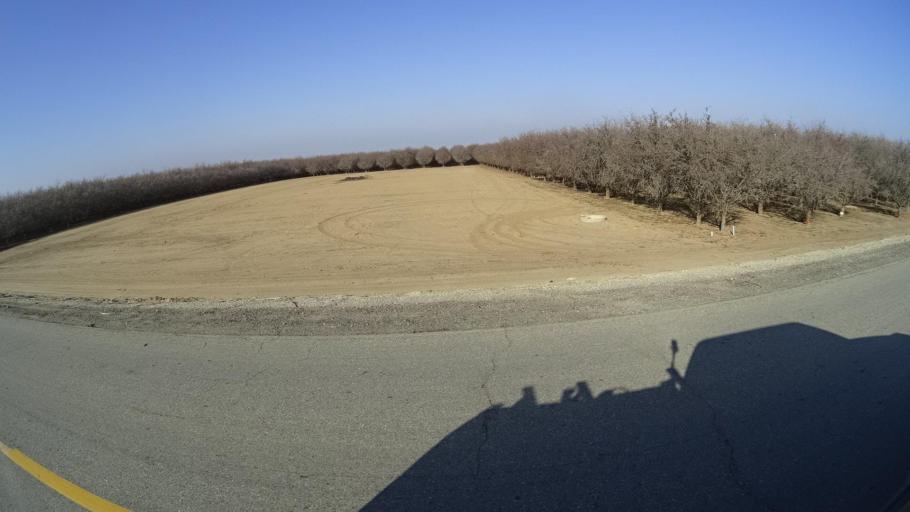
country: US
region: California
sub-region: Kern County
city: Maricopa
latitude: 35.1011
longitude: -119.3277
